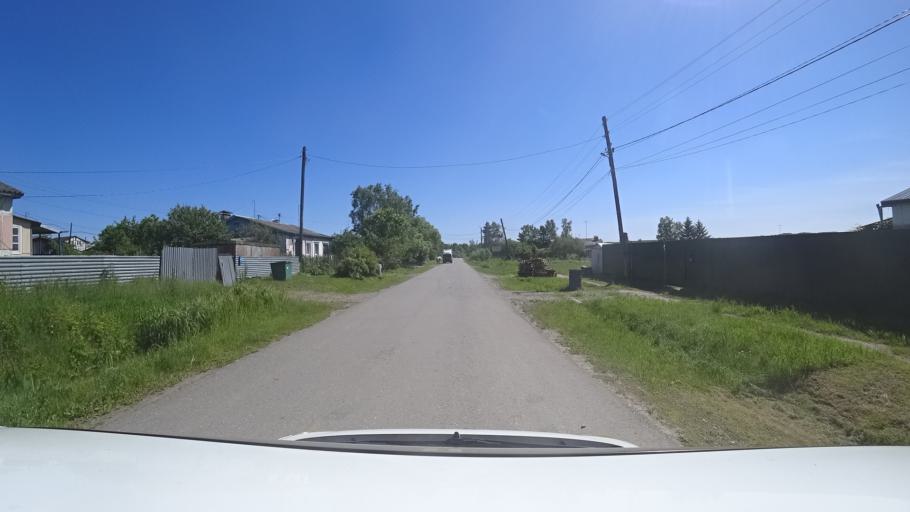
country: RU
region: Khabarovsk Krai
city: Topolevo
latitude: 48.5577
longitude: 135.1903
